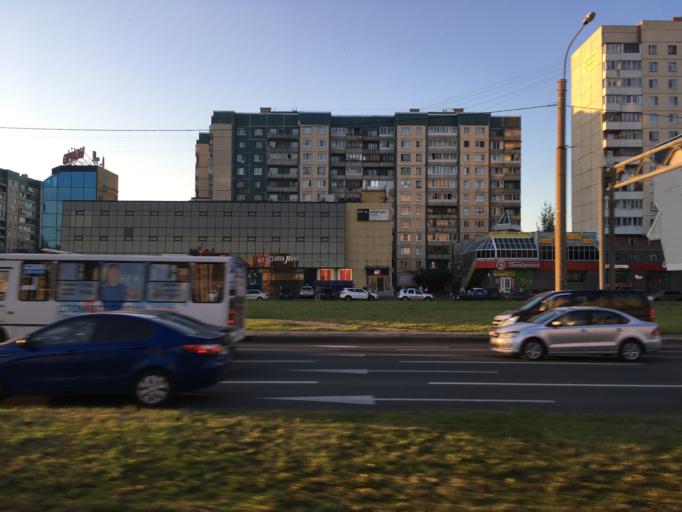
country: RU
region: St.-Petersburg
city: Komendantsky aerodrom
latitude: 60.0077
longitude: 30.2622
